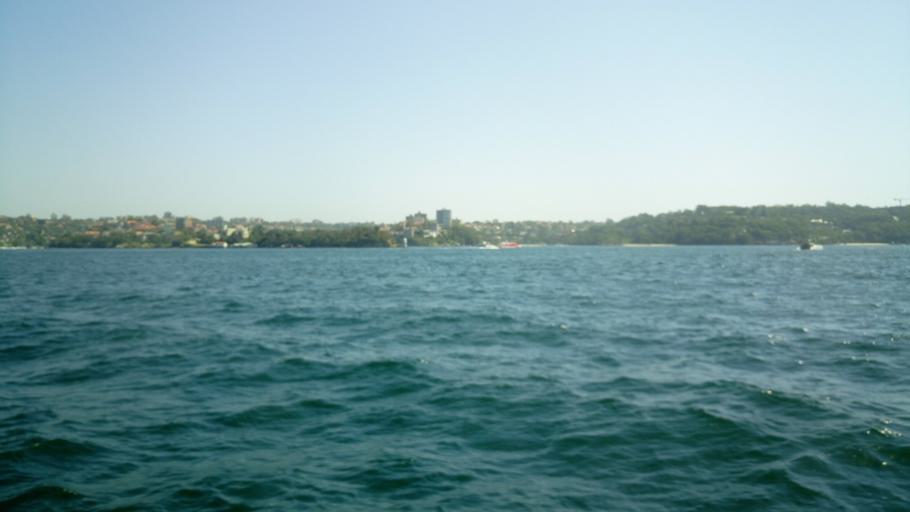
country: AU
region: New South Wales
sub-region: Woollahra
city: Darling Point
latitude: -33.8558
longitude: 151.2327
